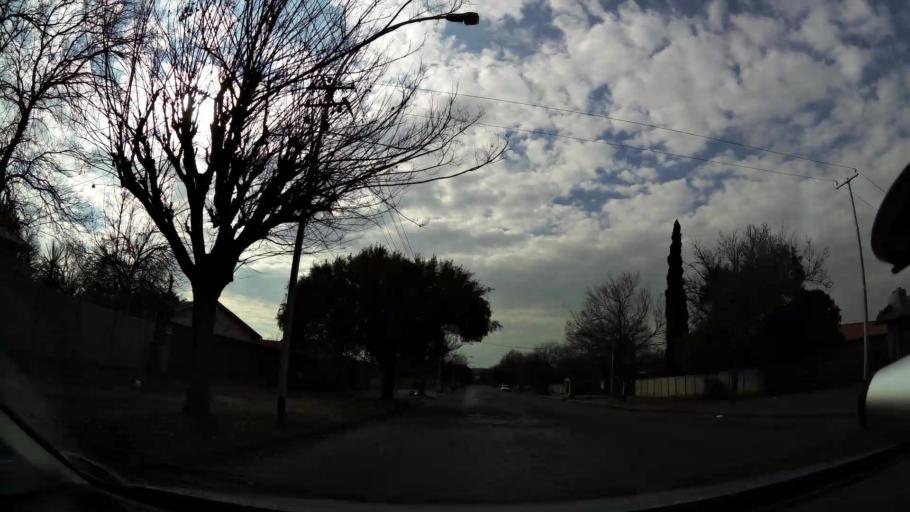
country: ZA
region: Orange Free State
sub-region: Mangaung Metropolitan Municipality
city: Bloemfontein
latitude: -29.0898
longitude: 26.2448
